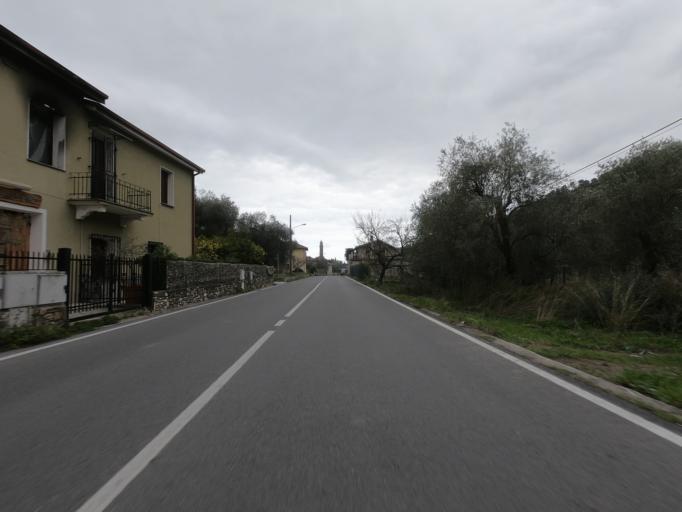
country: IT
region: Liguria
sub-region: Provincia di Savona
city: Villafranca
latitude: 43.9988
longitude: 8.1106
